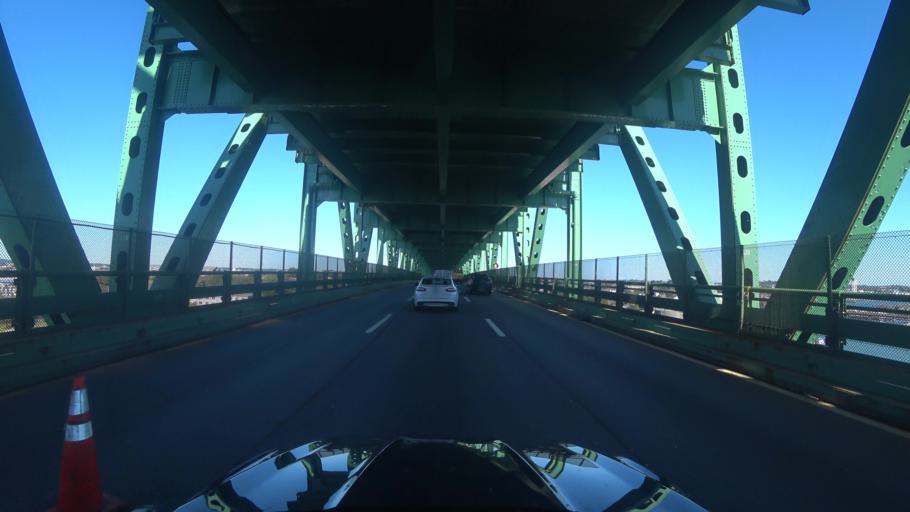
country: US
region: Massachusetts
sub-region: Suffolk County
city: Chelsea
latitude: 42.3835
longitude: -71.0485
